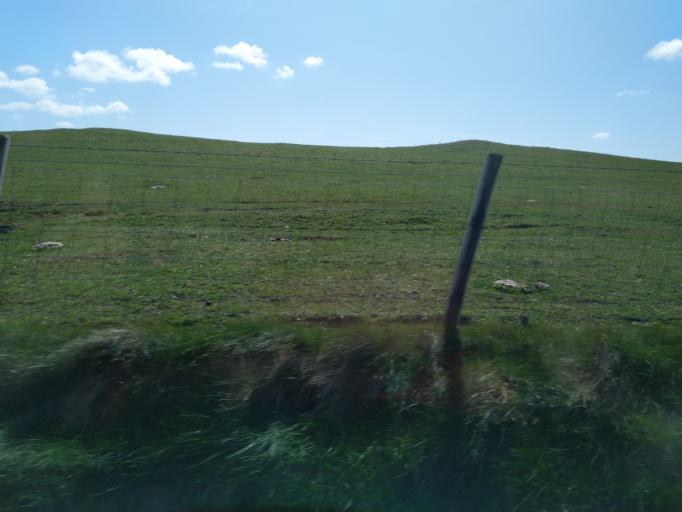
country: GB
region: Scotland
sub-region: Eilean Siar
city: Barra
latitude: 56.4833
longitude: -6.8896
